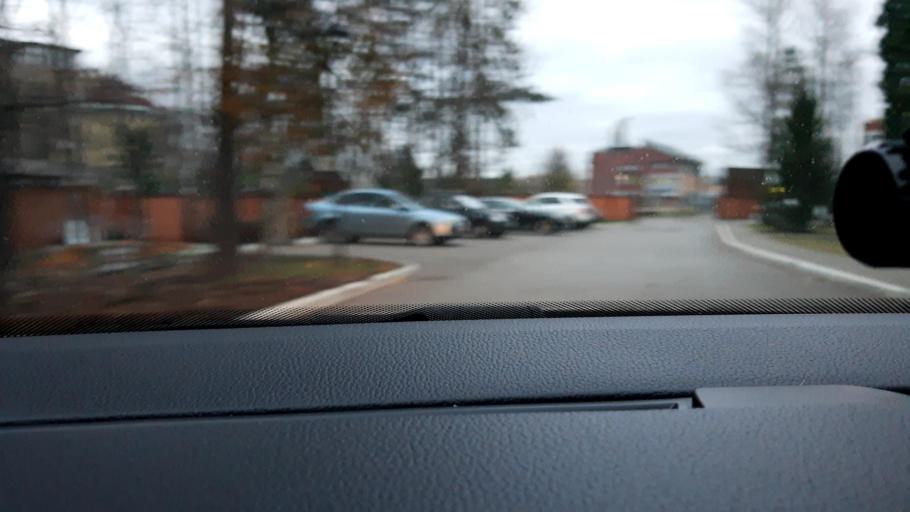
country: RU
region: Moskovskaya
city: Zarech'ye
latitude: 55.6803
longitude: 37.3856
